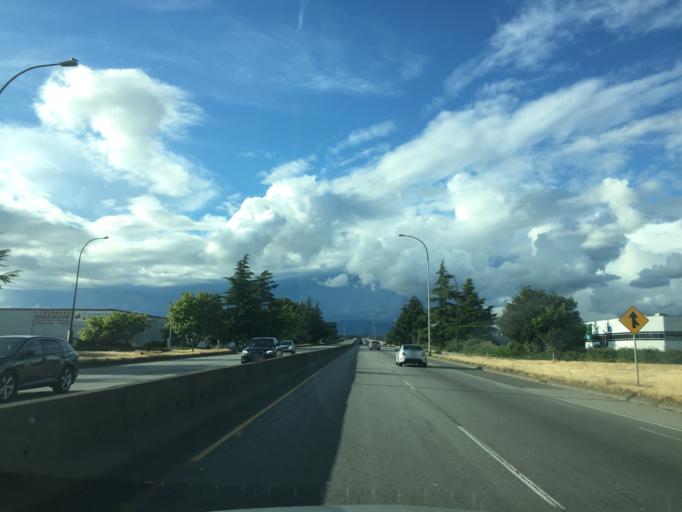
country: CA
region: British Columbia
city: Richmond
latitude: 49.1921
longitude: -123.0774
